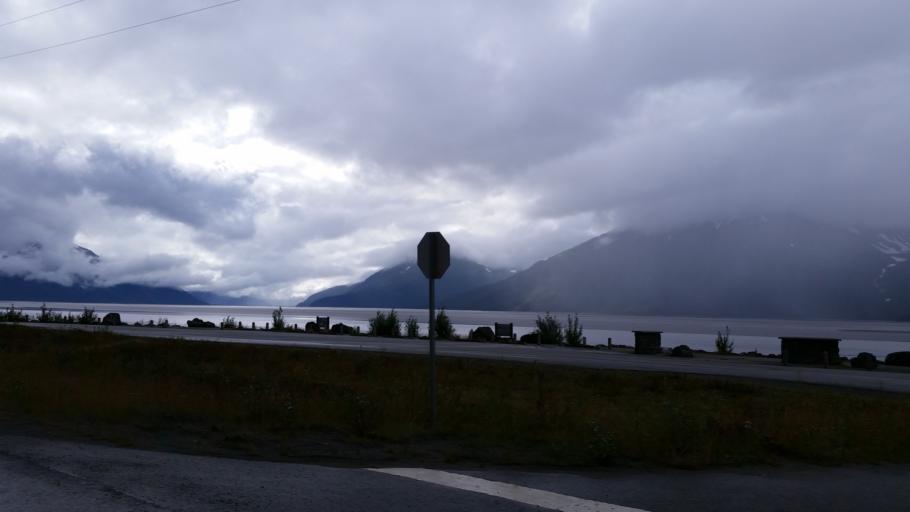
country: US
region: Alaska
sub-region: Anchorage Municipality
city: Girdwood
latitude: 60.9372
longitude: -149.2655
